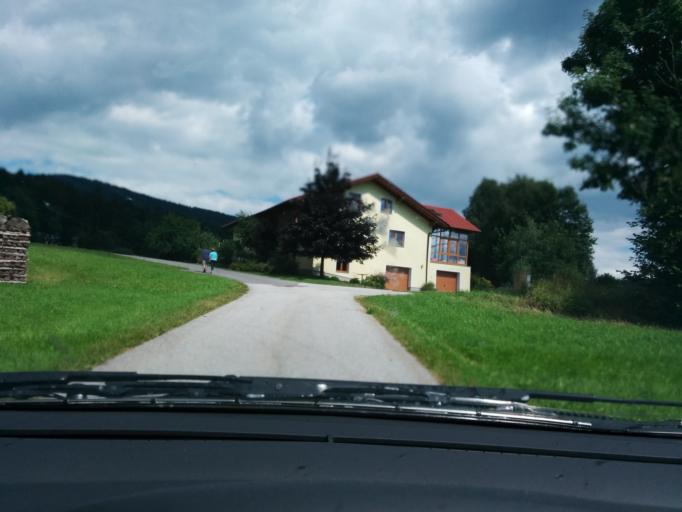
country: AT
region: Upper Austria
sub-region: Politischer Bezirk Rohrbach
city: Ulrichsberg
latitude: 48.7126
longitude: 13.9029
